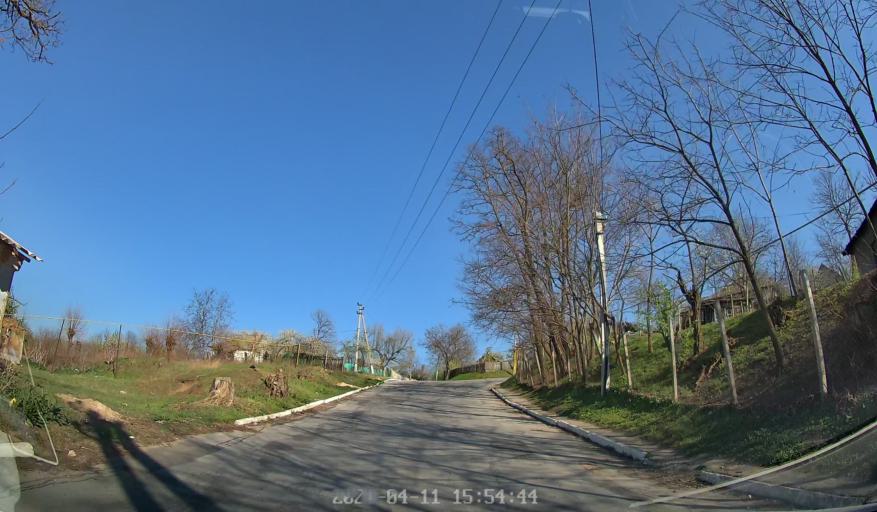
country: MD
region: Chisinau
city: Vadul lui Voda
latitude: 47.0982
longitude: 29.1766
